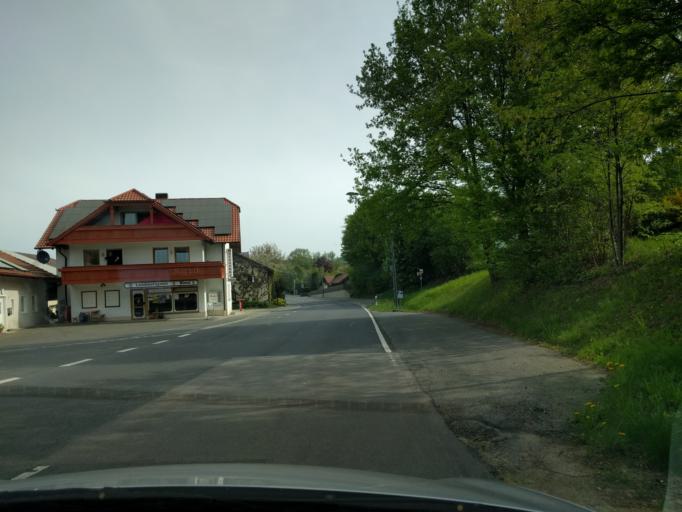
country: DE
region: Bavaria
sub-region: Upper Palatinate
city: Schorndorf
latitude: 49.1778
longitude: 12.6257
